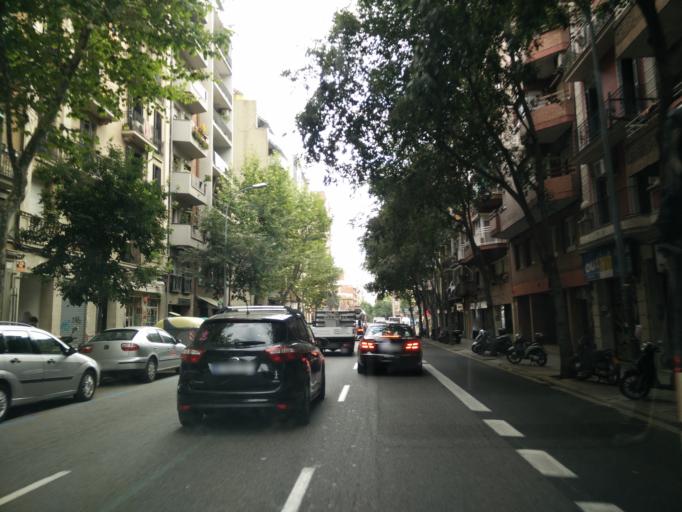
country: ES
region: Catalonia
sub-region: Provincia de Barcelona
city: Sant Marti
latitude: 41.4093
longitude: 2.1857
